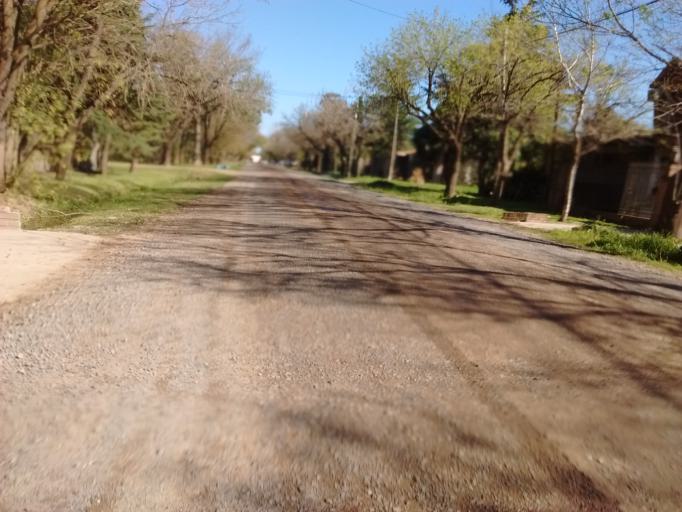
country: AR
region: Santa Fe
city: Funes
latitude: -32.9248
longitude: -60.8153
